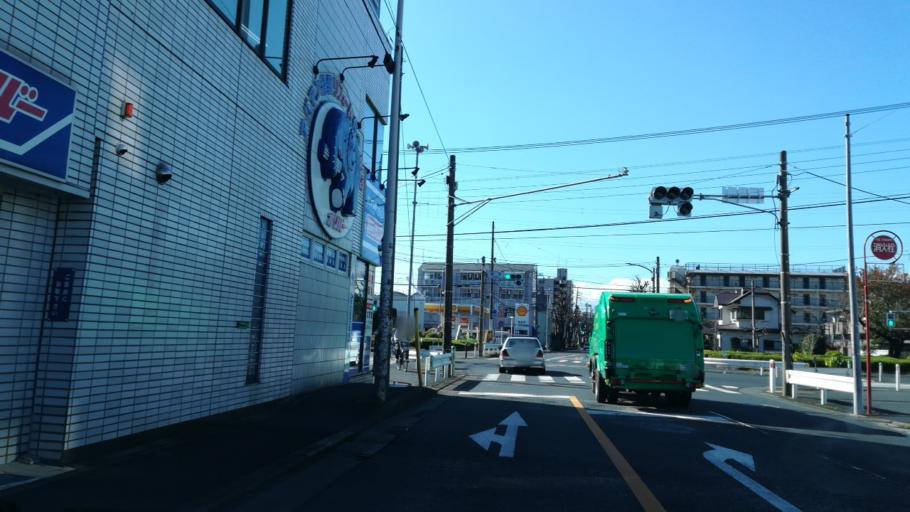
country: JP
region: Tokyo
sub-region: Machida-shi
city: Machida
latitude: 35.5693
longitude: 139.3894
